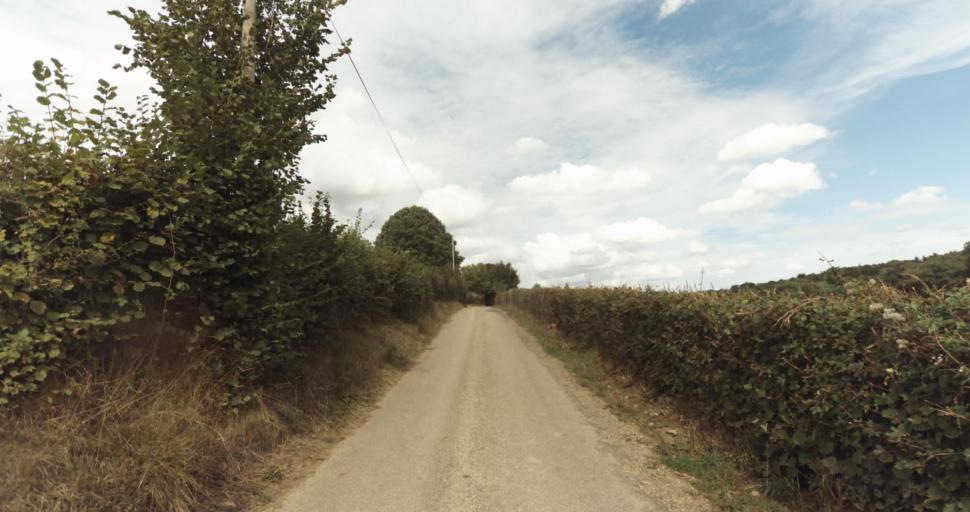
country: FR
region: Lower Normandy
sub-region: Departement du Calvados
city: Orbec
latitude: 48.9043
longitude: 0.3755
